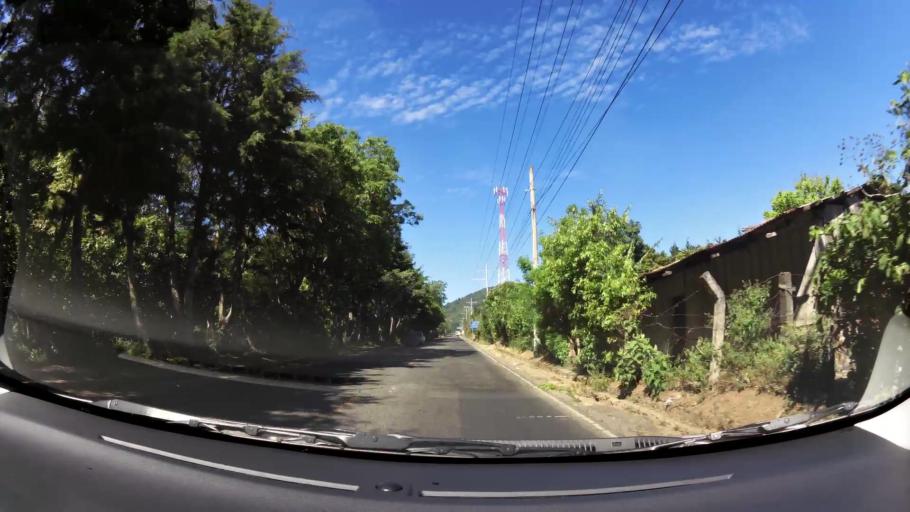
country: SV
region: Ahuachapan
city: Concepcion de Ataco
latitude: 13.8630
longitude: -89.7967
